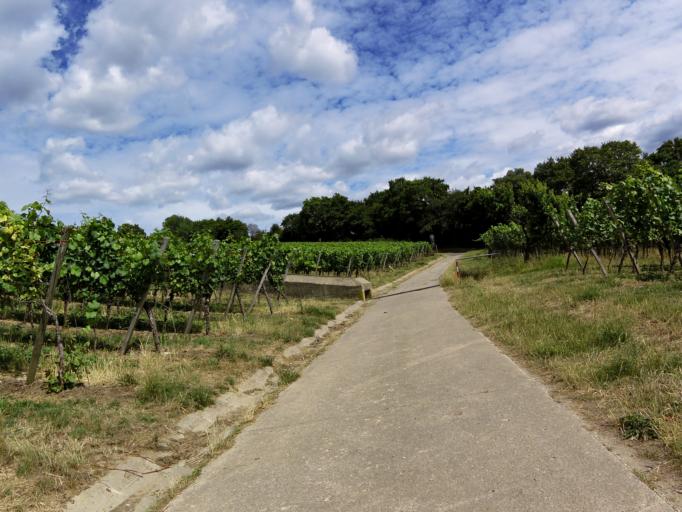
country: DE
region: Bavaria
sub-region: Regierungsbezirk Unterfranken
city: Veitshochheim
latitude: 49.8159
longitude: 9.8934
